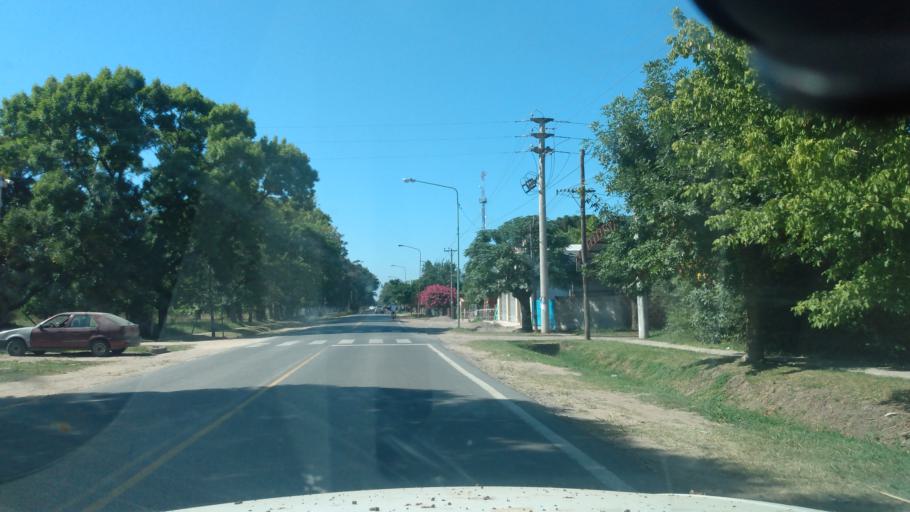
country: AR
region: Buenos Aires
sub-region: Partido de Lujan
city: Lujan
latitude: -34.4957
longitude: -59.0743
